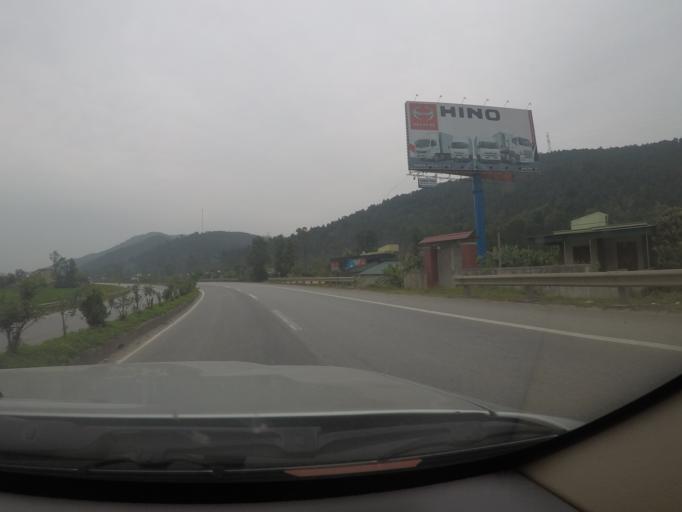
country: VN
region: Nghe An
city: Quan Hanh
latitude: 18.8726
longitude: 105.6175
